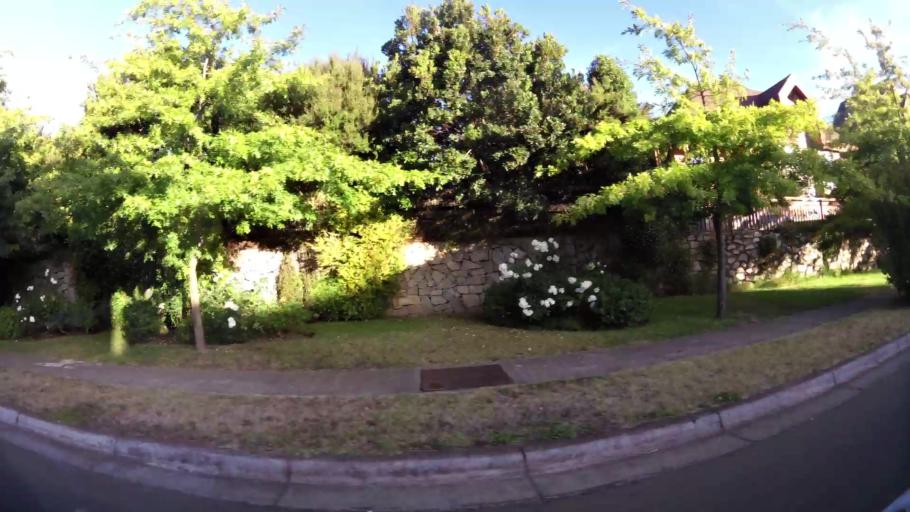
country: CL
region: Biobio
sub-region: Provincia de Concepcion
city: Concepcion
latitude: -36.8618
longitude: -73.0998
